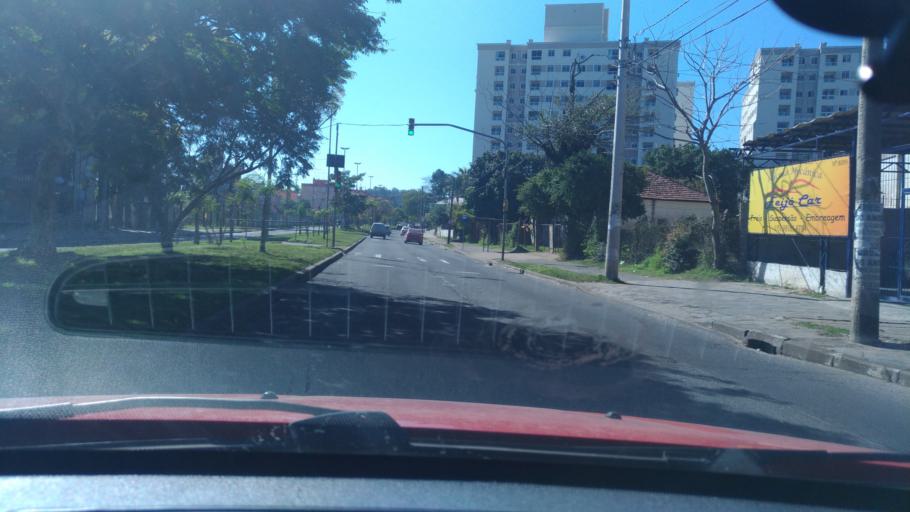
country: BR
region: Rio Grande do Sul
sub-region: Cachoeirinha
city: Cachoeirinha
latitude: -30.0411
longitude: -51.1310
